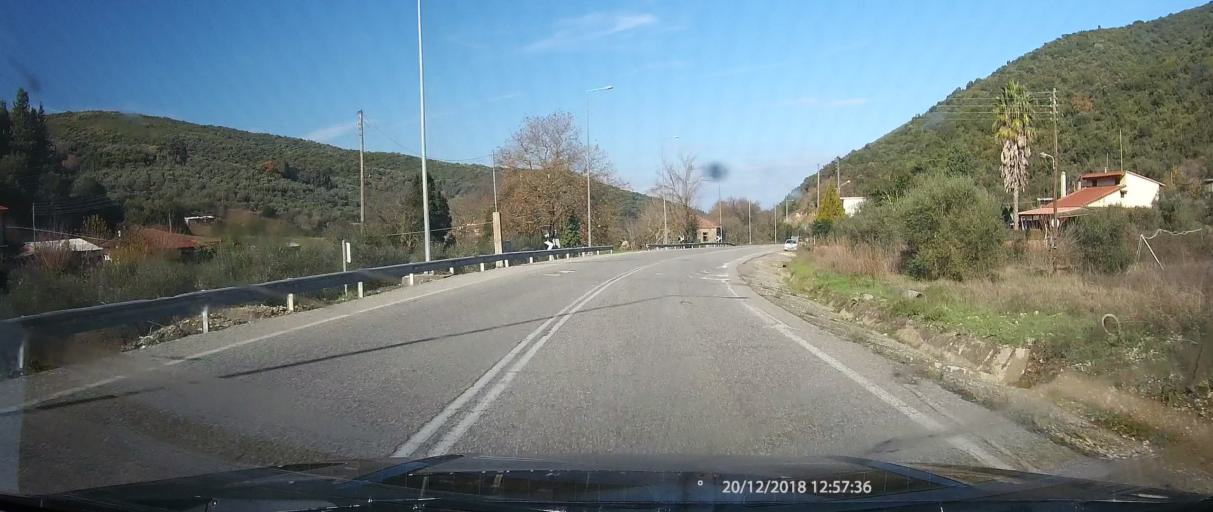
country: GR
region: West Greece
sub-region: Nomos Aitolias kai Akarnanias
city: Pappadhatai
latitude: 38.5255
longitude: 21.3765
